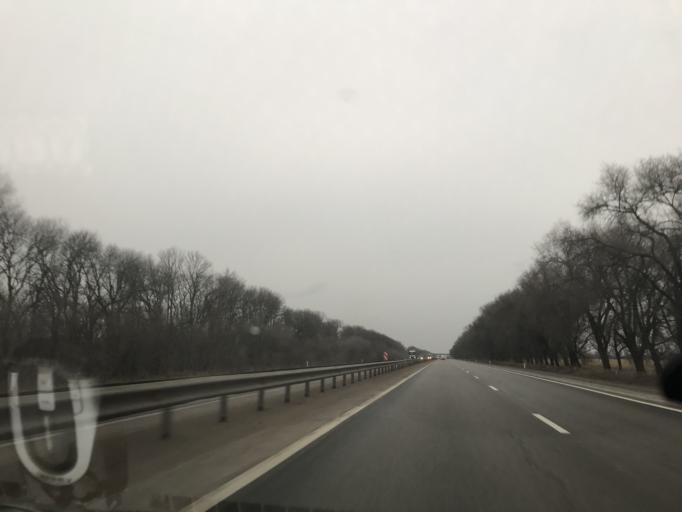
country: RU
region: Krasnodarskiy
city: Pavlovskaya
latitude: 46.1959
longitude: 39.8317
